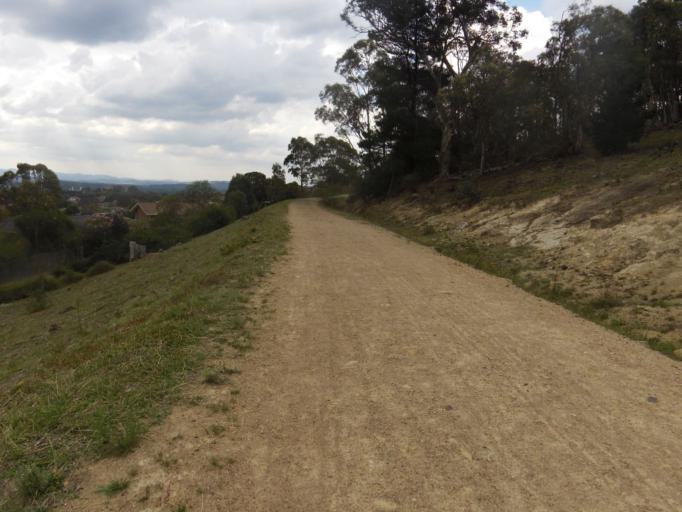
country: AU
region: Australian Capital Territory
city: Macarthur
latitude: -35.3623
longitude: 149.1132
